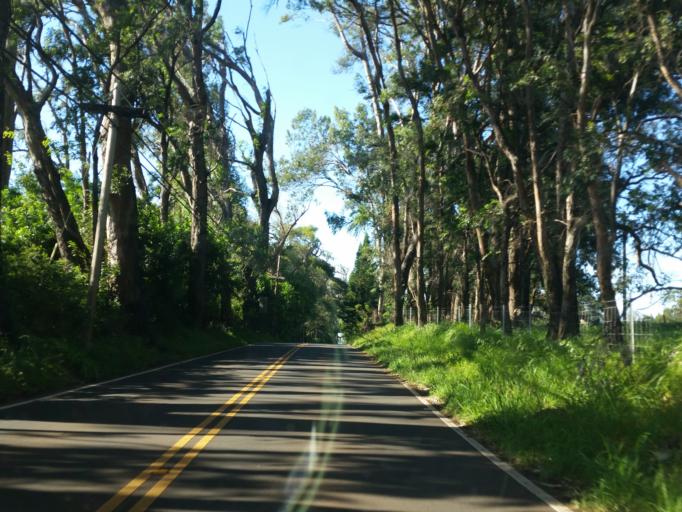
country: US
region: Hawaii
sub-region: Maui County
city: Makawao
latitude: 20.8417
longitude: -156.3089
